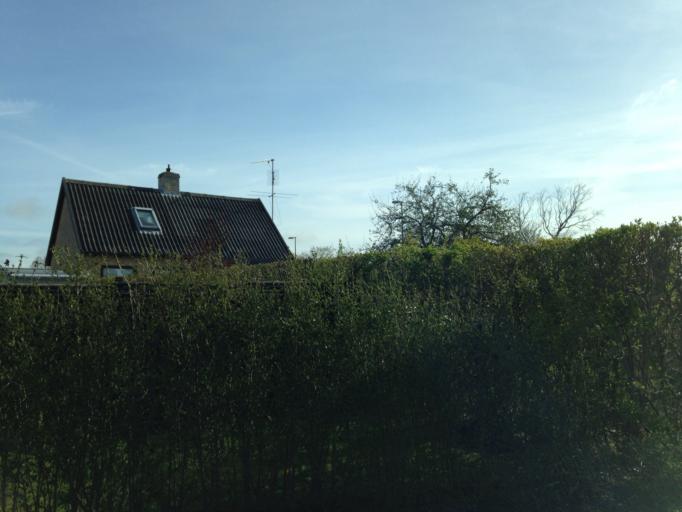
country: DK
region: Zealand
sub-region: Greve Kommune
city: Greve
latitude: 55.5867
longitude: 12.2978
